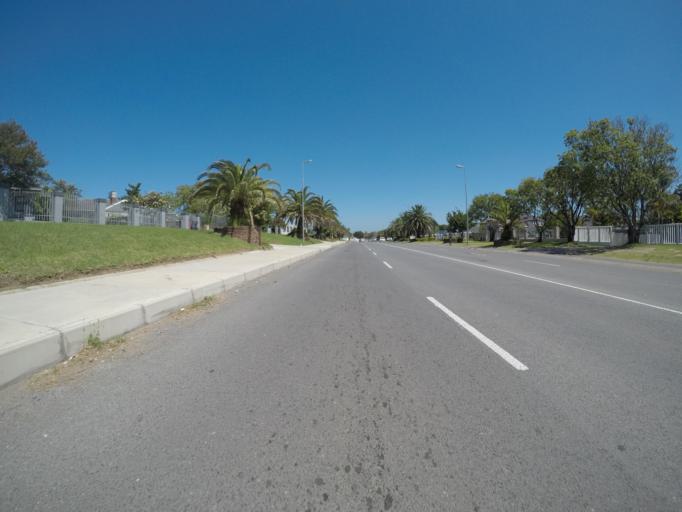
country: ZA
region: Eastern Cape
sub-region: Buffalo City Metropolitan Municipality
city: East London
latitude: -32.9659
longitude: 27.9375
